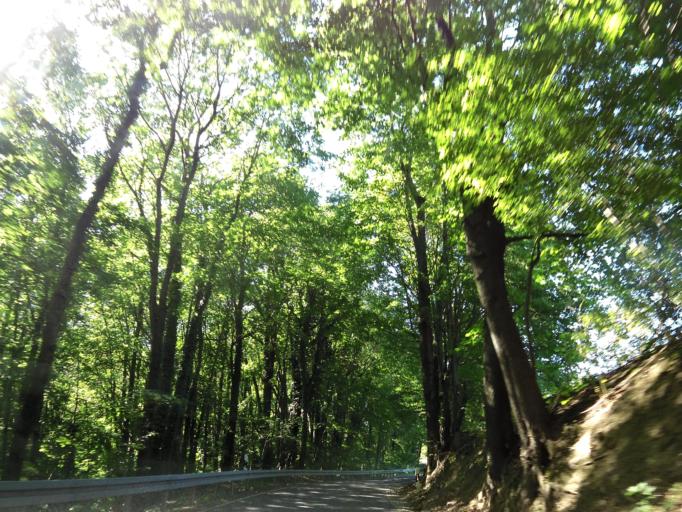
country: DE
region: Saxony
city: Dohna
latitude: 50.9262
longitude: 13.8147
